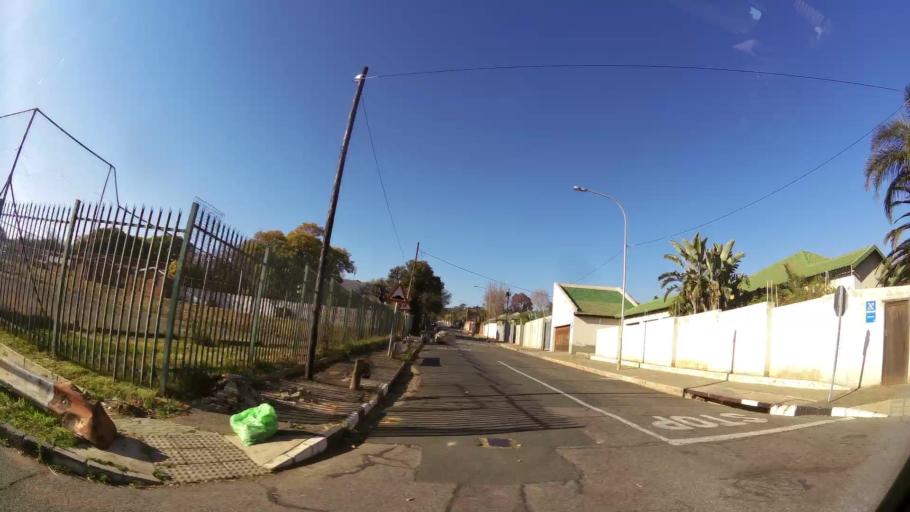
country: ZA
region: Gauteng
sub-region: City of Johannesburg Metropolitan Municipality
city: Johannesburg
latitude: -26.1887
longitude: 28.0999
